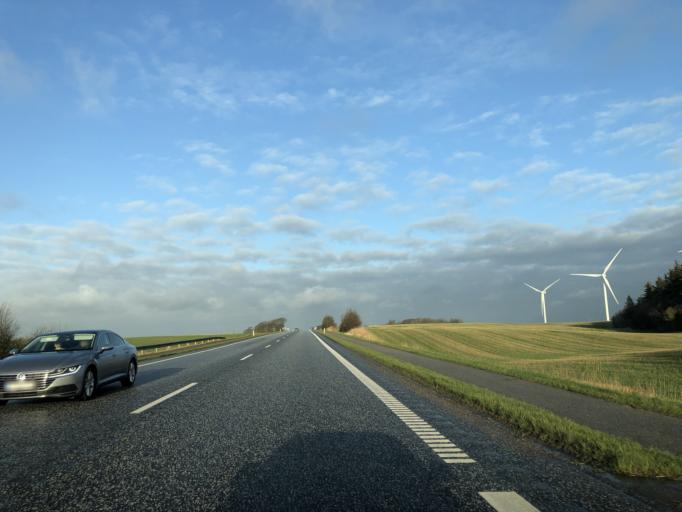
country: DK
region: Central Jutland
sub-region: Holstebro Kommune
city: Holstebro
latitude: 56.4174
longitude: 8.6021
